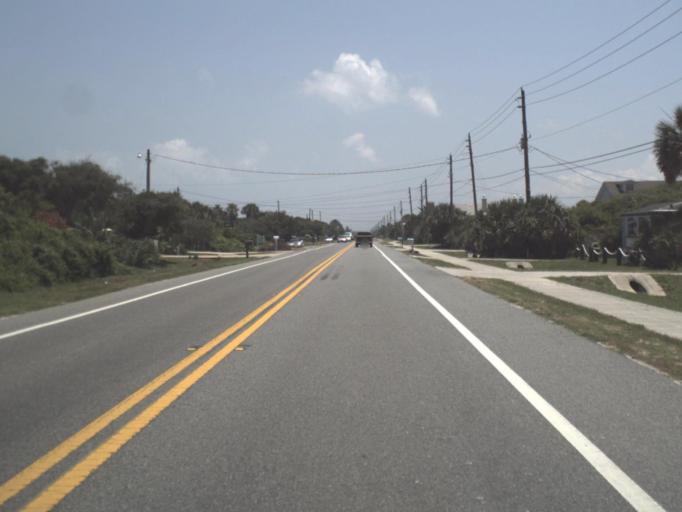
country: US
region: Florida
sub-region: Saint Johns County
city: Butler Beach
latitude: 29.7659
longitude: -81.2524
